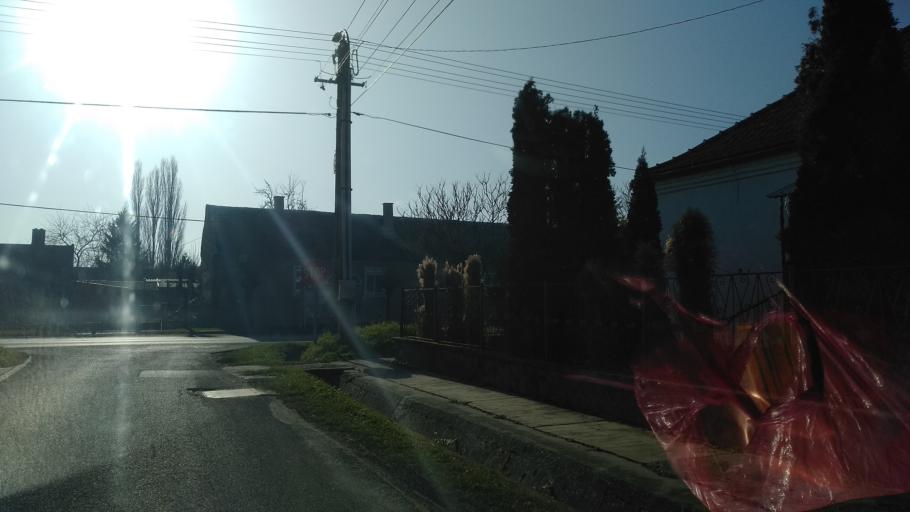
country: HU
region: Somogy
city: Barcs
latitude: 45.9621
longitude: 17.4824
